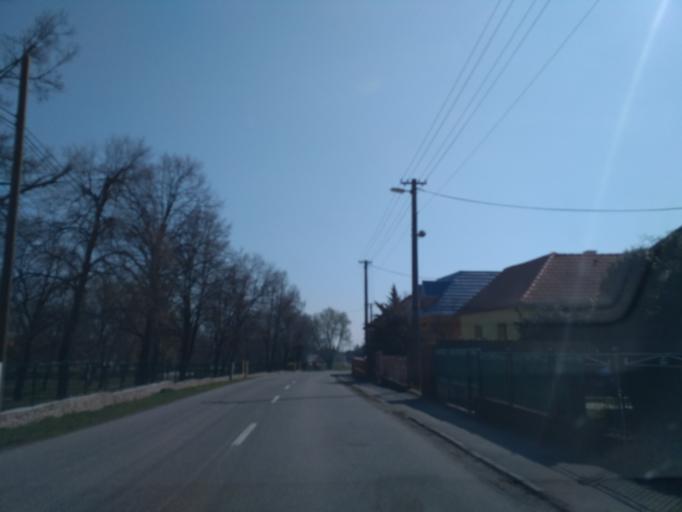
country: SK
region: Kosicky
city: Secovce
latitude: 48.7388
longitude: 21.6255
